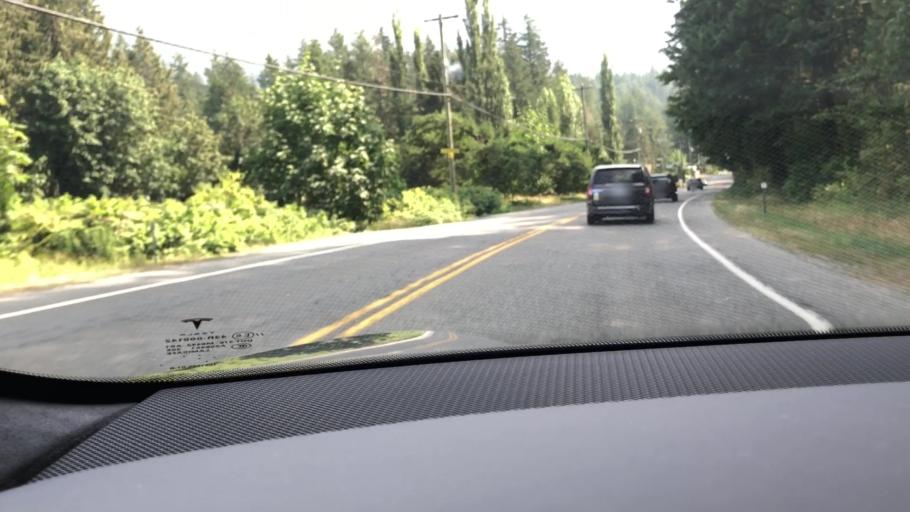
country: CA
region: British Columbia
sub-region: Fraser Valley Regional District
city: Chilliwack
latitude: 49.0725
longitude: -121.9624
